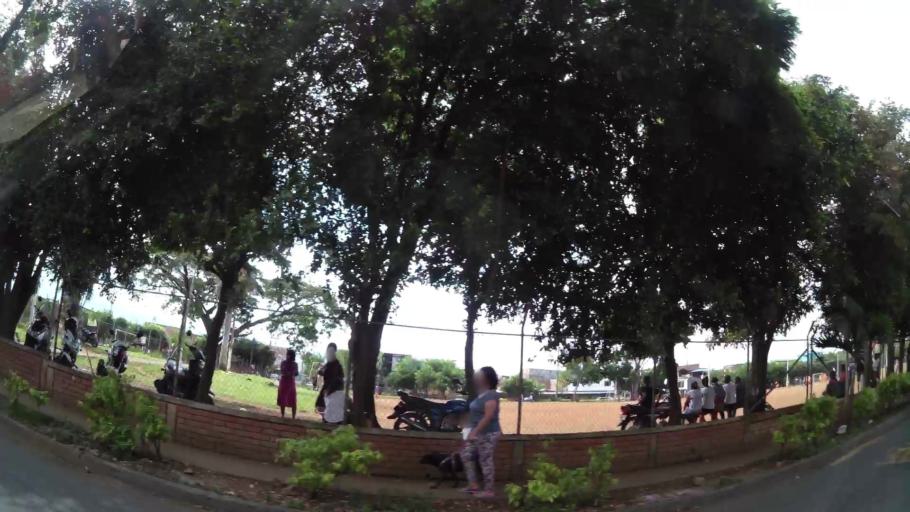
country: CO
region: Valle del Cauca
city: Cali
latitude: 3.3990
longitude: -76.5103
